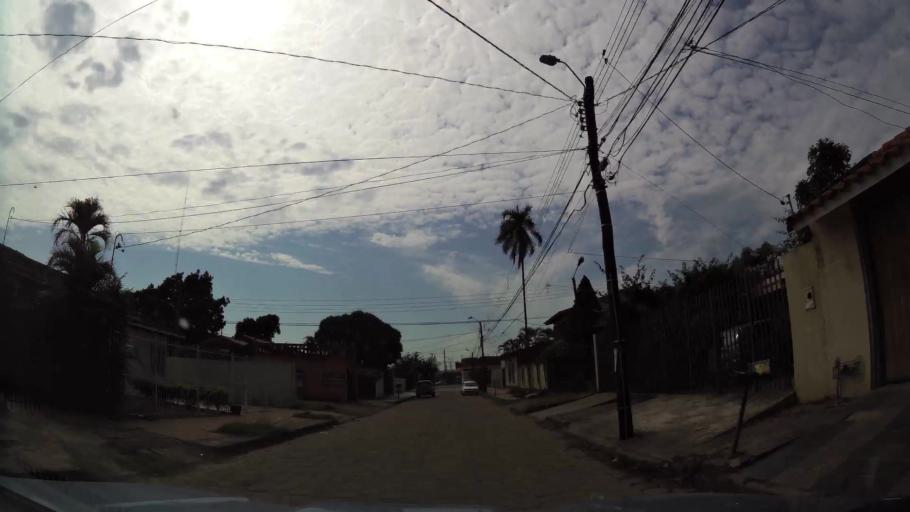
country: BO
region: Santa Cruz
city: Santa Cruz de la Sierra
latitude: -17.7479
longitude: -63.1540
